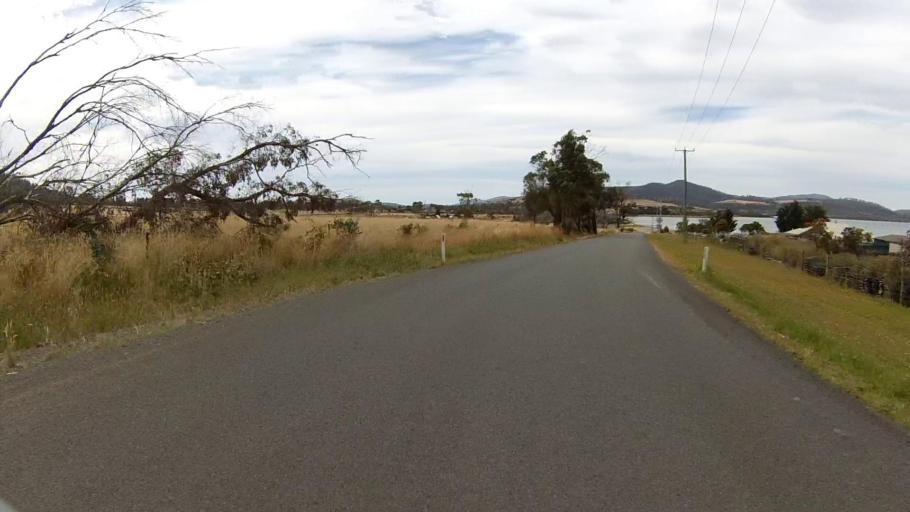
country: AU
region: Tasmania
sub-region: Sorell
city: Sorell
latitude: -42.8910
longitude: 147.7911
